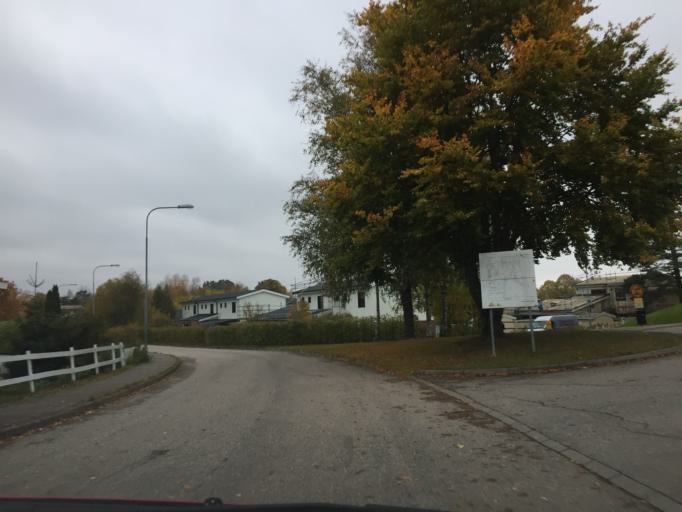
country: SE
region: Vaestra Goetaland
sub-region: Trollhattan
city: Trollhattan
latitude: 58.2562
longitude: 12.2990
